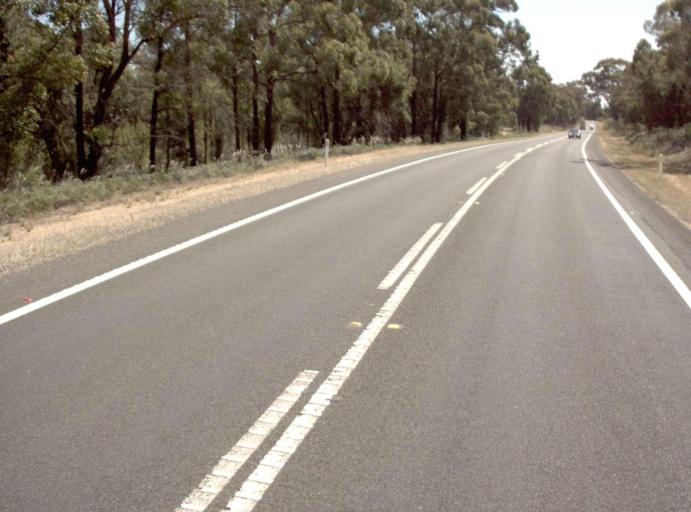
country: AU
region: Victoria
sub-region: Wellington
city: Sale
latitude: -37.9150
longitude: 147.2986
